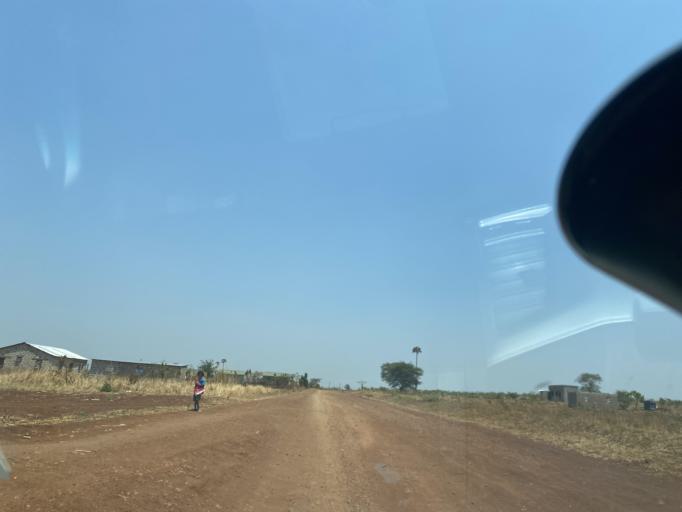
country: ZM
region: Lusaka
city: Kafue
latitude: -15.5174
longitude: 27.9389
